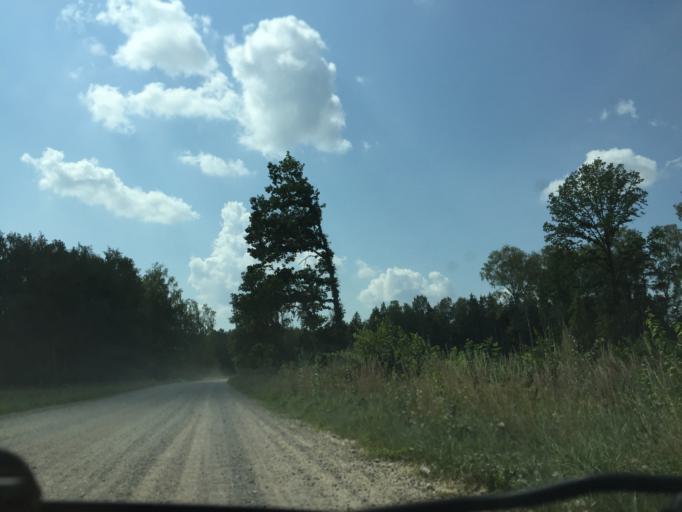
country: LV
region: Tervete
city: Zelmeni
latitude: 56.3976
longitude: 23.3212
